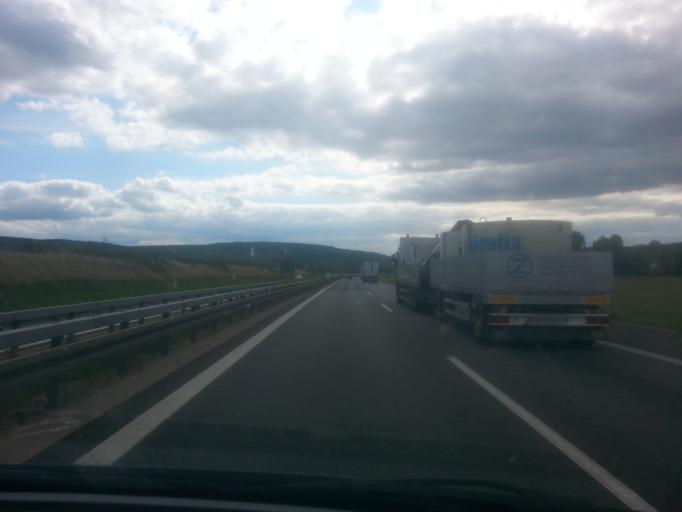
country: DE
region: Bavaria
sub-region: Upper Palatinate
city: Nabburg
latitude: 49.4471
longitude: 12.1906
